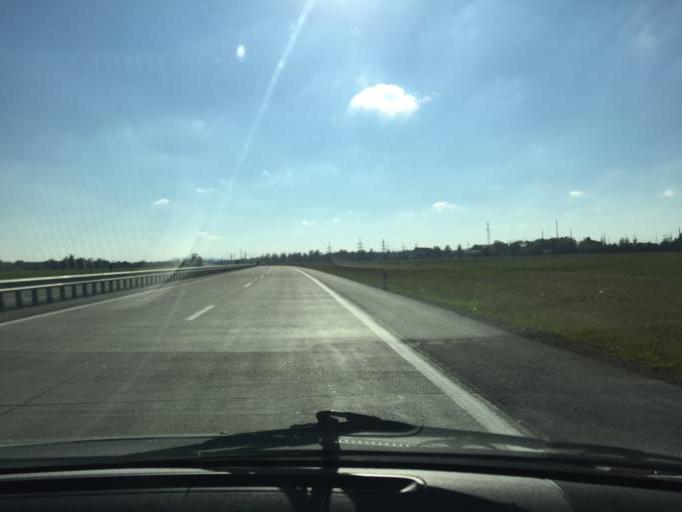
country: BY
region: Minsk
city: Slutsk
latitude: 53.0264
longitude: 27.4843
